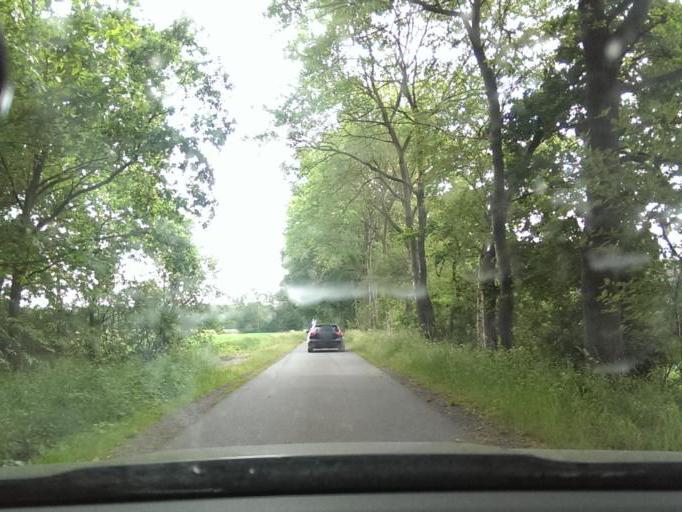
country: DE
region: Lower Saxony
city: Lindwedel
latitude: 52.5338
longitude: 9.6595
